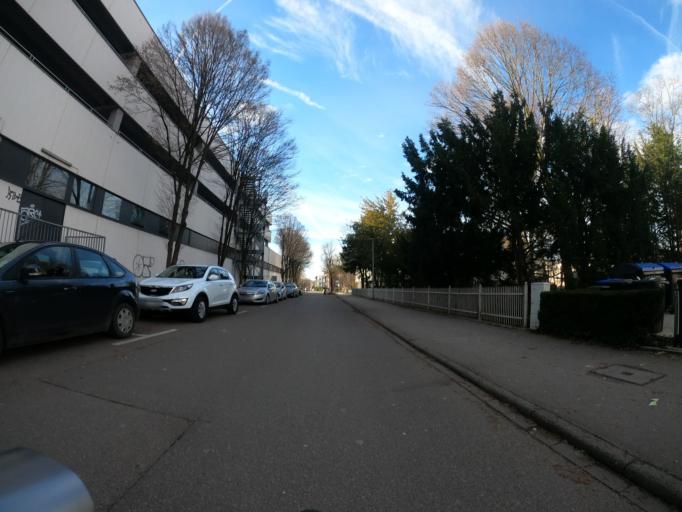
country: DE
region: Baden-Wuerttemberg
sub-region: Regierungsbezirk Stuttgart
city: Kirchheim unter Teck
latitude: 48.6501
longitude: 9.4452
